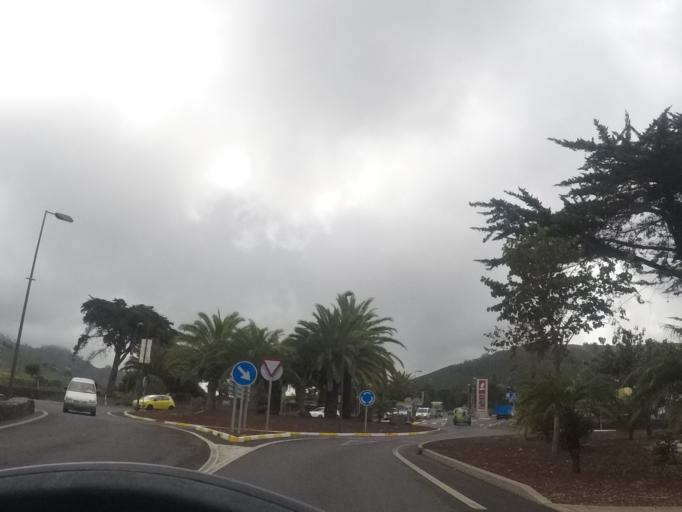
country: ES
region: Canary Islands
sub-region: Provincia de Santa Cruz de Tenerife
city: Tegueste
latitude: 28.5208
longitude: -16.3362
